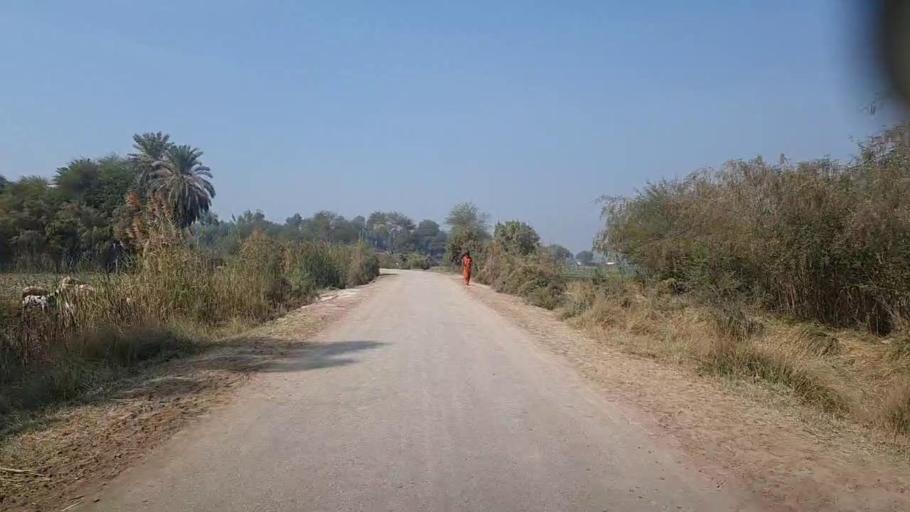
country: PK
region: Sindh
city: Khairpur
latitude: 27.9643
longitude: 69.6666
